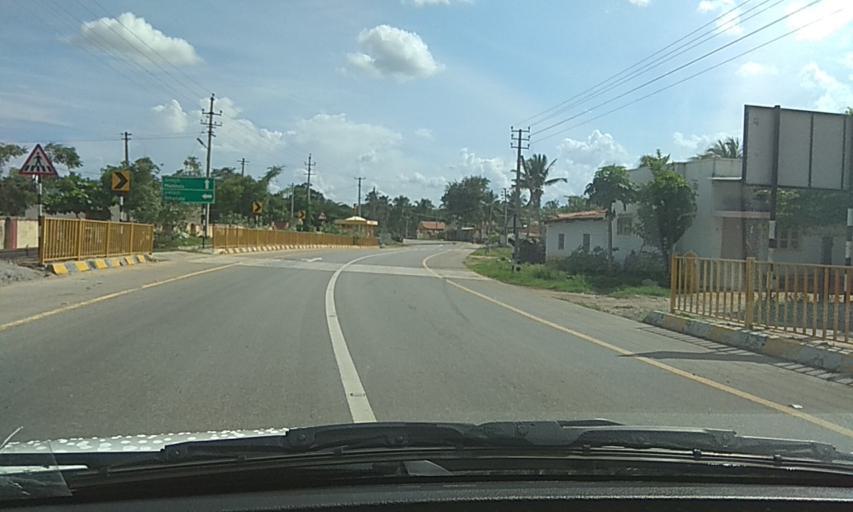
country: IN
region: Karnataka
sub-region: Mandya
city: Maddur
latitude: 12.6647
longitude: 77.0538
